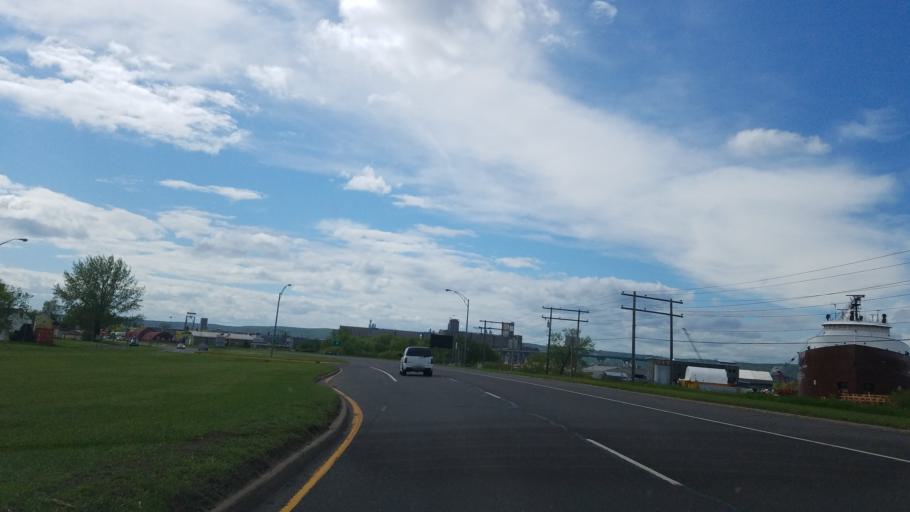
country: US
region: Wisconsin
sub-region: Douglas County
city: Superior
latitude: 46.7330
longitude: -92.0860
